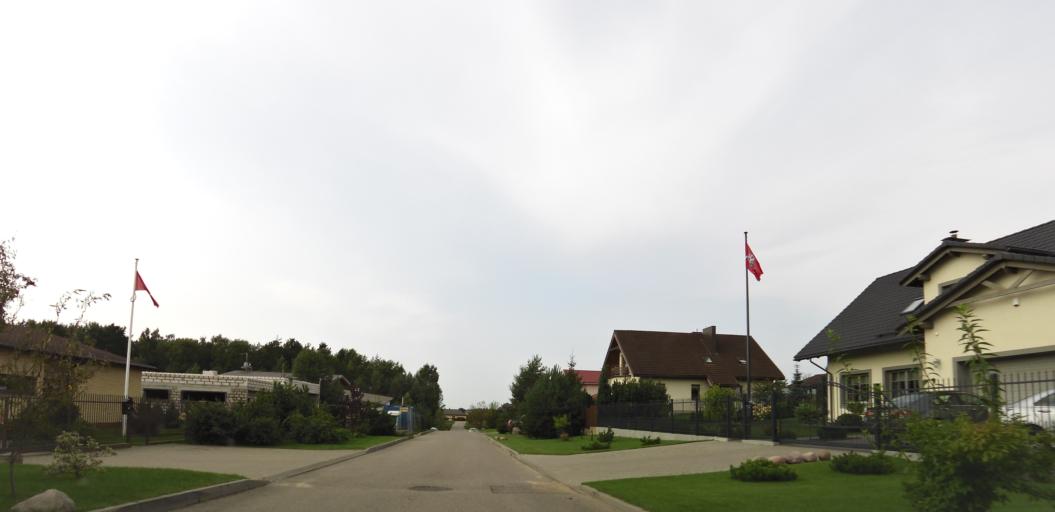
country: LT
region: Vilnius County
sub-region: Vilnius
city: Fabijoniskes
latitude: 54.7533
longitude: 25.2344
